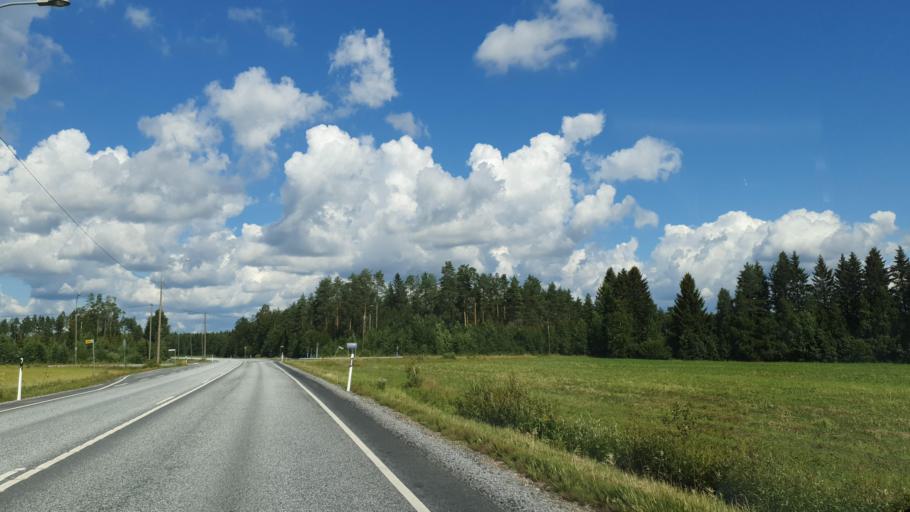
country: FI
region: Northern Savo
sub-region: Ylae-Savo
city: Sonkajaervi
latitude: 63.8791
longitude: 27.4412
